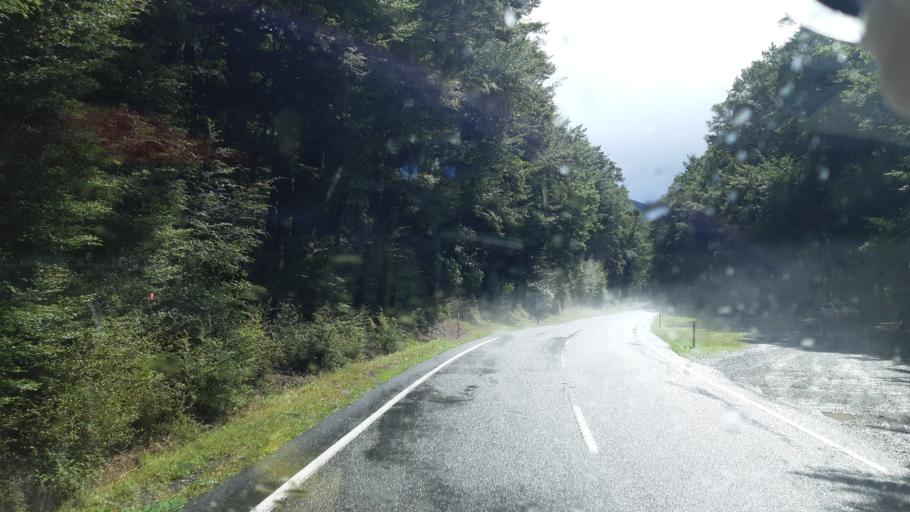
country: NZ
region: Canterbury
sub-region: Hurunui District
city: Amberley
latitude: -42.3789
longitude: 172.2780
